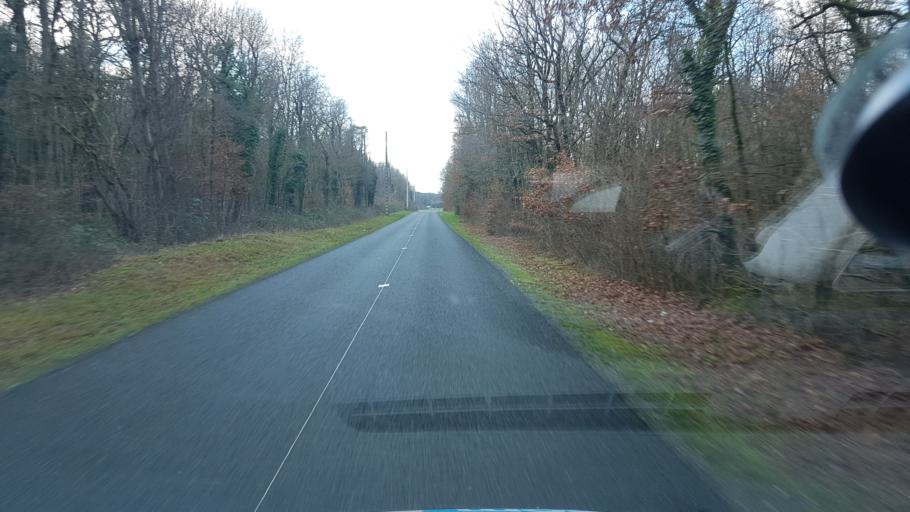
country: FR
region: Ile-de-France
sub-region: Departement de Seine-et-Marne
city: Montigny-sur-Loing
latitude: 48.2759
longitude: 2.7717
